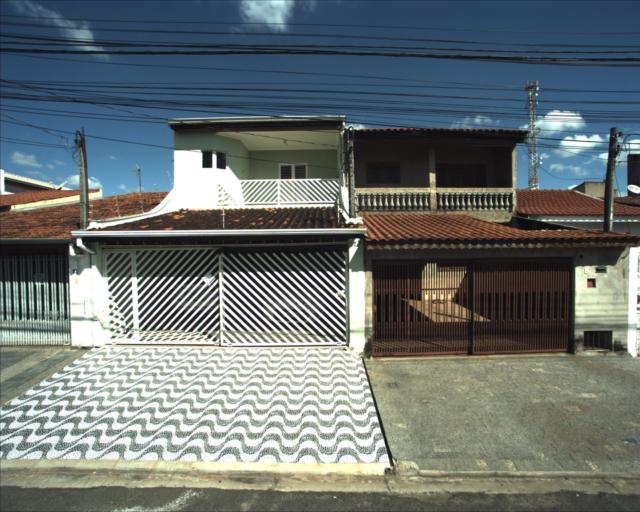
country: BR
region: Sao Paulo
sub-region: Sorocaba
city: Sorocaba
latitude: -23.4760
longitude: -47.4736
